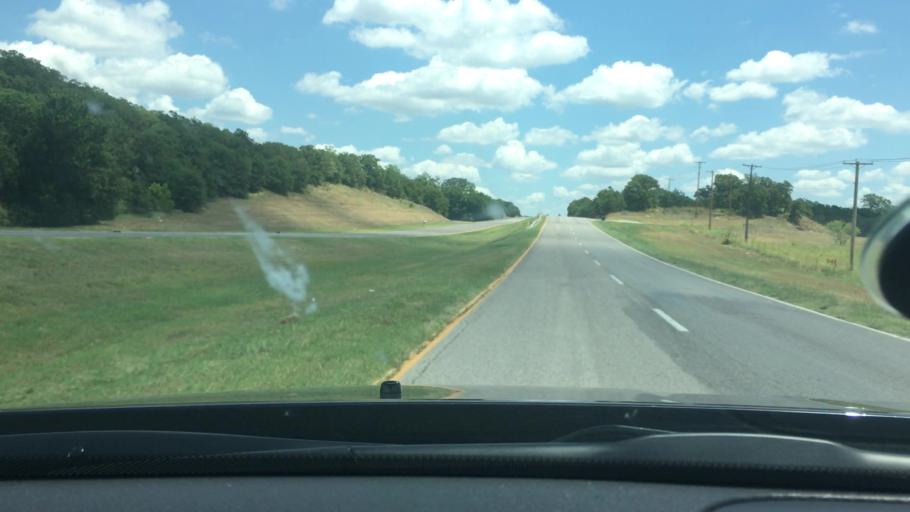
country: US
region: Oklahoma
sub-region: Carter County
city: Wilson
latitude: 34.1728
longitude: -97.3546
